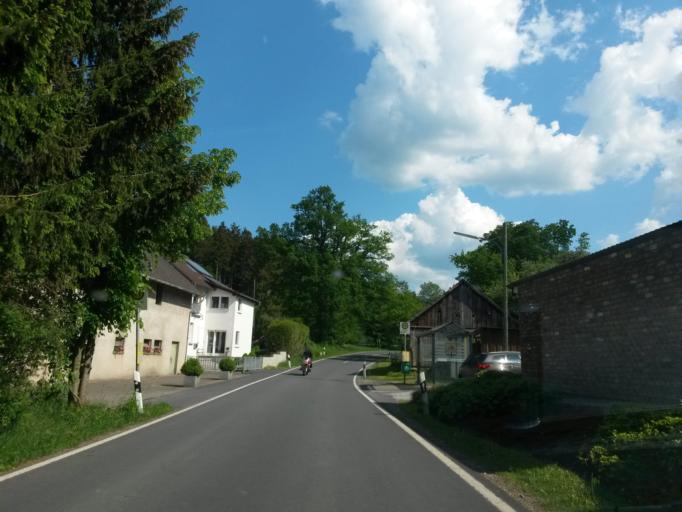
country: DE
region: North Rhine-Westphalia
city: Balve
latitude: 51.2874
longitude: 7.8476
